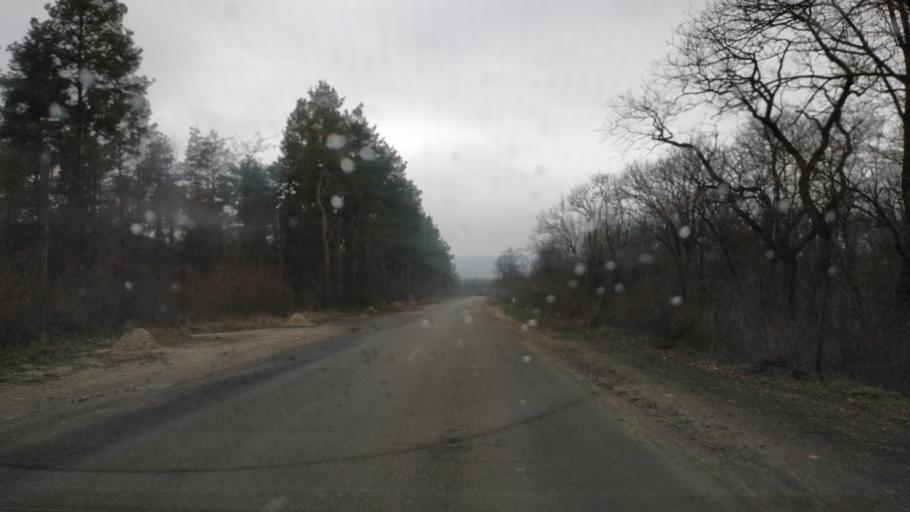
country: MD
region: Cantemir
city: Iargara
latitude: 46.3677
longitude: 28.3861
